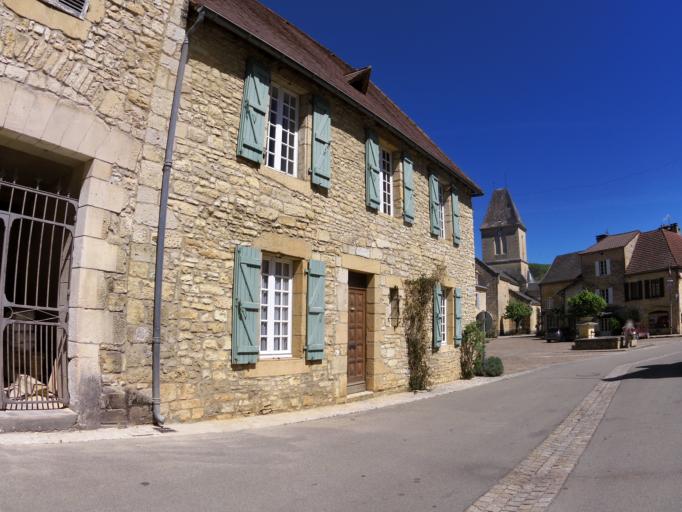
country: FR
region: Aquitaine
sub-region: Departement de la Dordogne
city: Cenac-et-Saint-Julien
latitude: 44.7424
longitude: 1.1912
